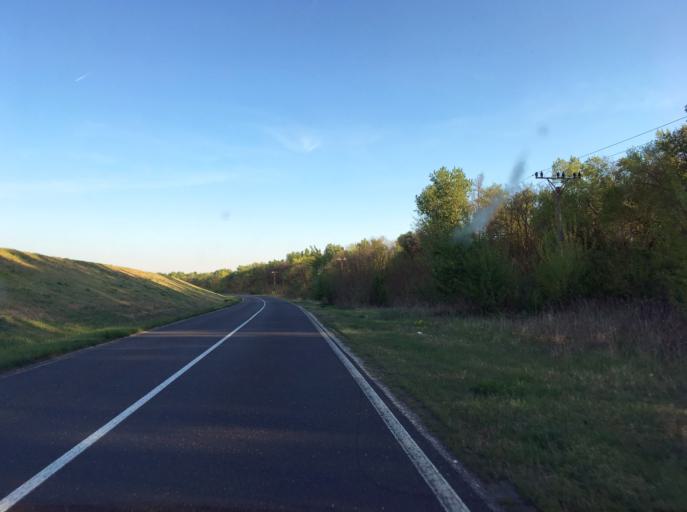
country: HU
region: Gyor-Moson-Sopron
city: Rajka
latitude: 48.0063
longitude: 17.2528
